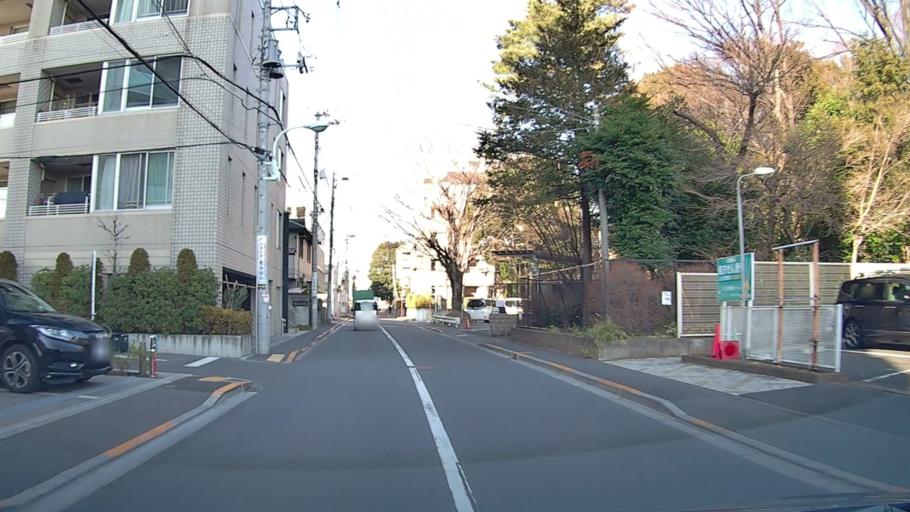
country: JP
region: Tokyo
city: Tokyo
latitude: 35.7170
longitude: 139.6361
